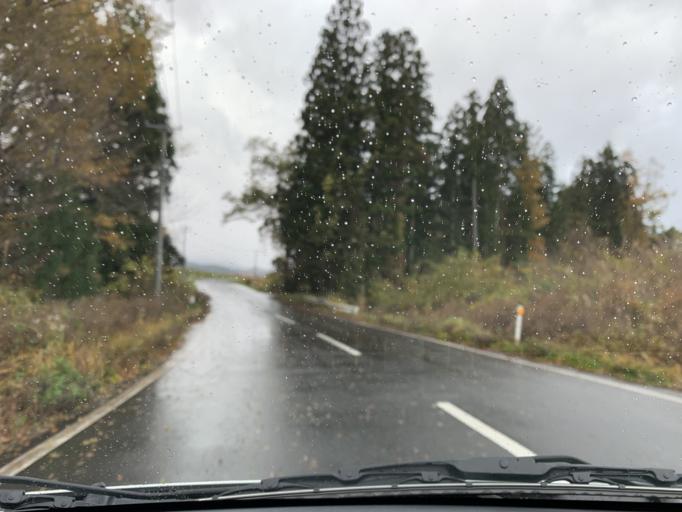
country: JP
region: Iwate
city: Mizusawa
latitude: 39.0891
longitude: 141.0050
